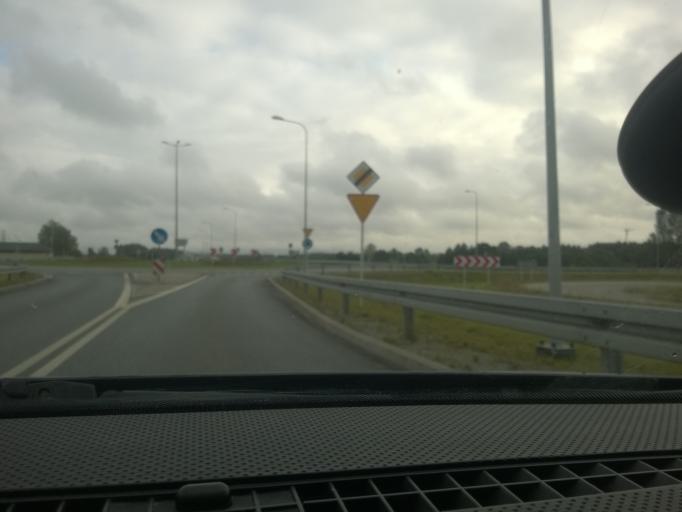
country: PL
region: Lodz Voivodeship
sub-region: Powiat sieradzki
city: Sieradz
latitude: 51.5691
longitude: 18.7008
